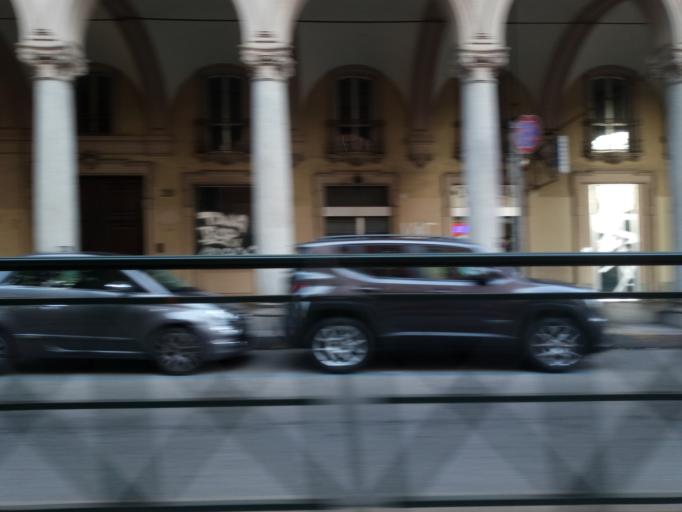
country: IT
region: Piedmont
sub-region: Provincia di Torino
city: Turin
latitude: 45.0608
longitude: 7.6758
